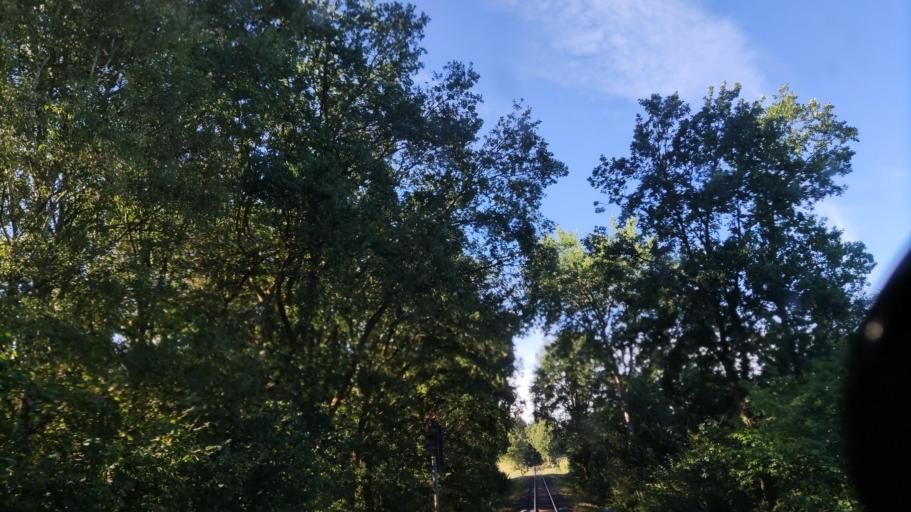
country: DE
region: Lower Saxony
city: Embsen
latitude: 53.1778
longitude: 10.3687
